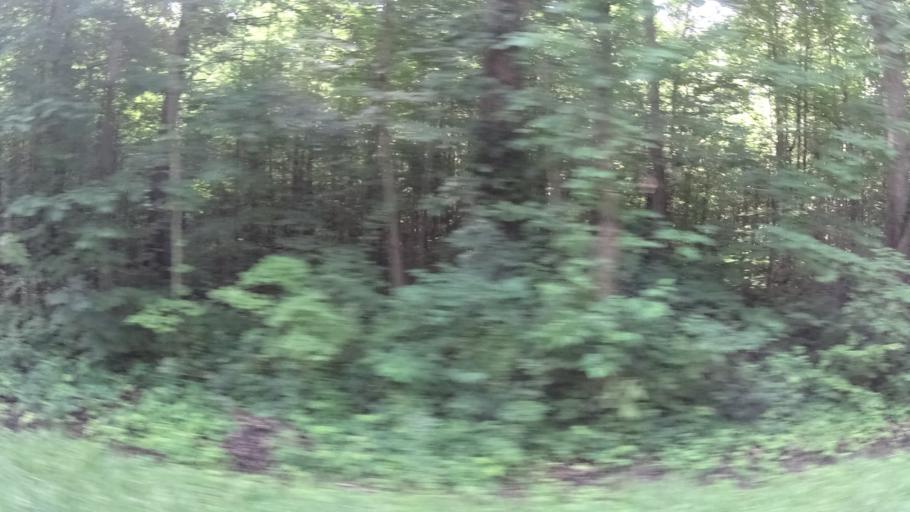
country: US
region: Ohio
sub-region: Huron County
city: Wakeman
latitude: 41.2839
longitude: -82.4297
